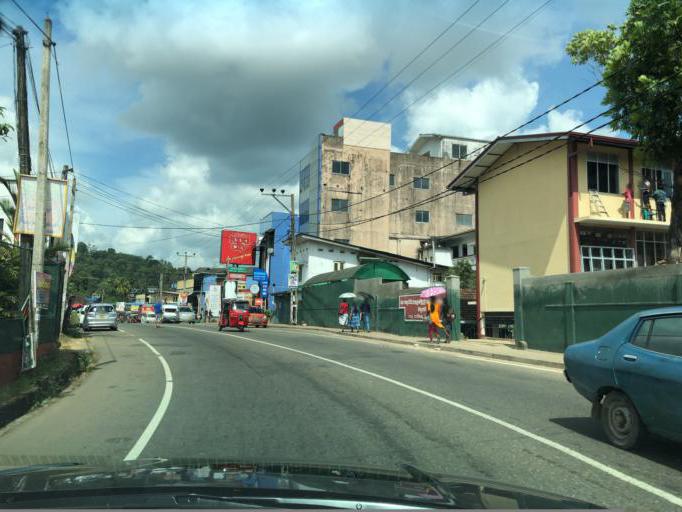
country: LK
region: Western
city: Horawala Junction
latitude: 6.5222
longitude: 80.1113
